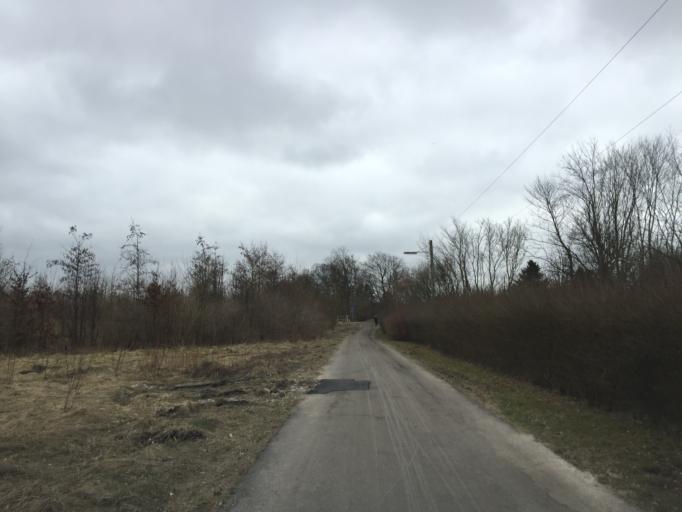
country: DK
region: Capital Region
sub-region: Allerod Kommune
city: Lillerod
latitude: 55.9007
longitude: 12.3309
